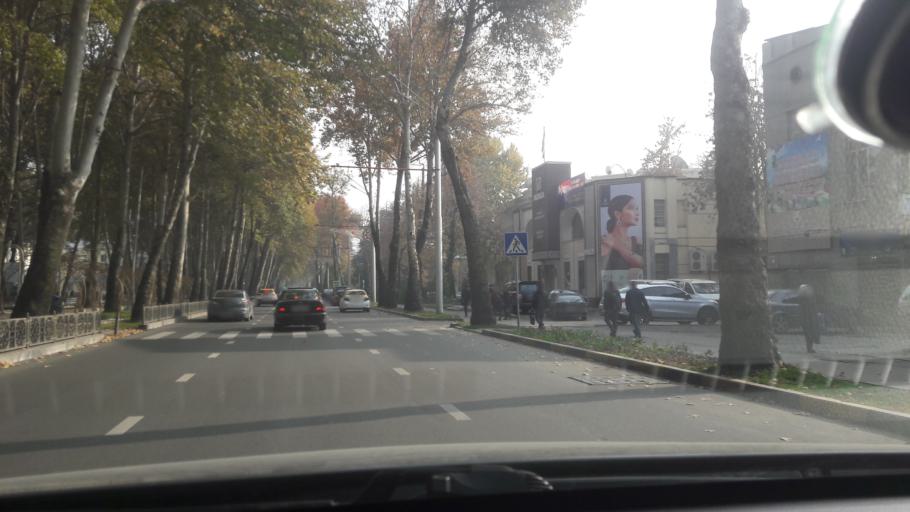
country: TJ
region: Dushanbe
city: Dushanbe
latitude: 38.5707
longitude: 68.7899
